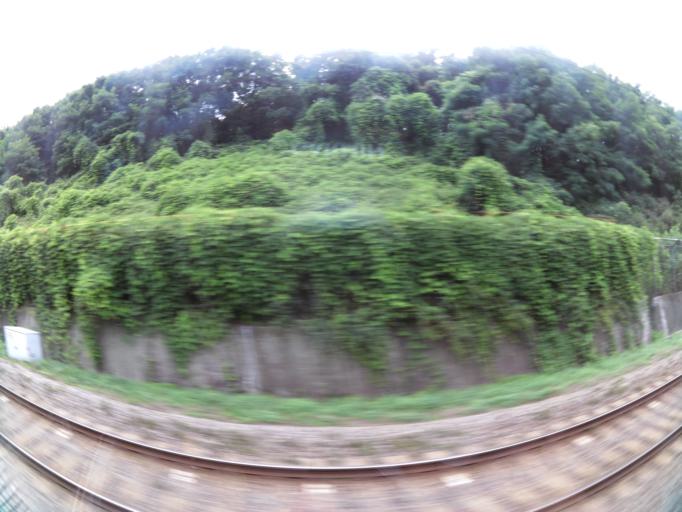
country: KR
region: Gyeonggi-do
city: Osan
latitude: 37.1835
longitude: 127.0468
